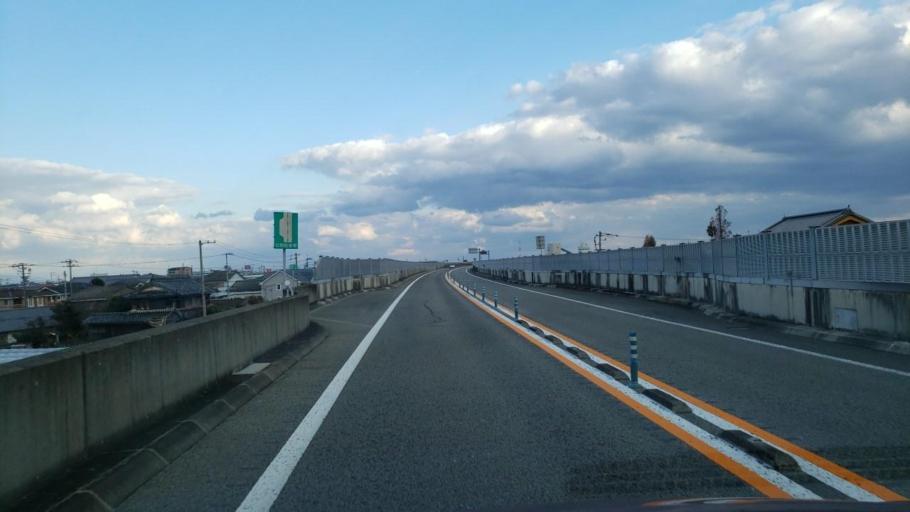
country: JP
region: Tokushima
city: Ishii
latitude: 34.1174
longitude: 134.4844
